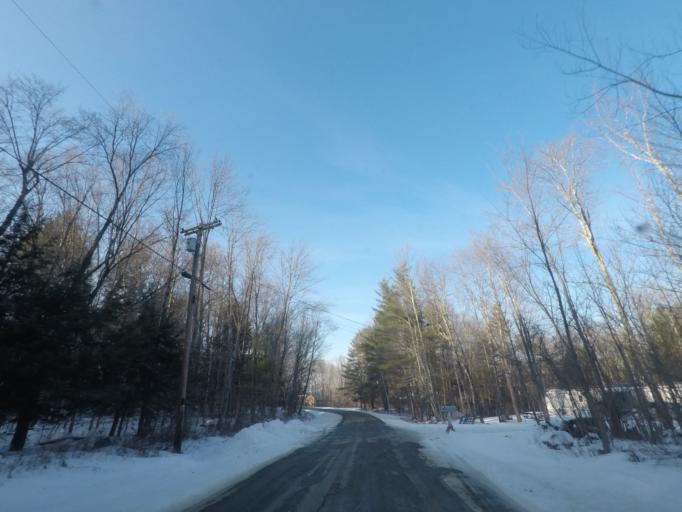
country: US
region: New York
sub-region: Rensselaer County
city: Nassau
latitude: 42.5011
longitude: -73.5044
